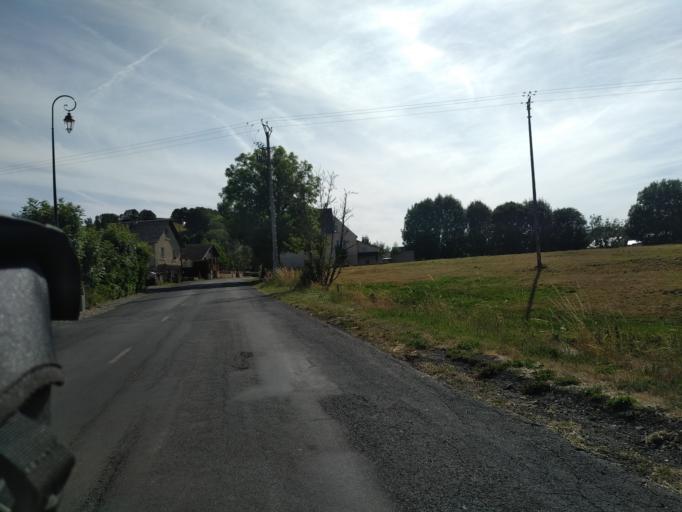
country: FR
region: Auvergne
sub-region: Departement du Cantal
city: Chaudes-Aigues
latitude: 44.6634
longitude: 3.0519
